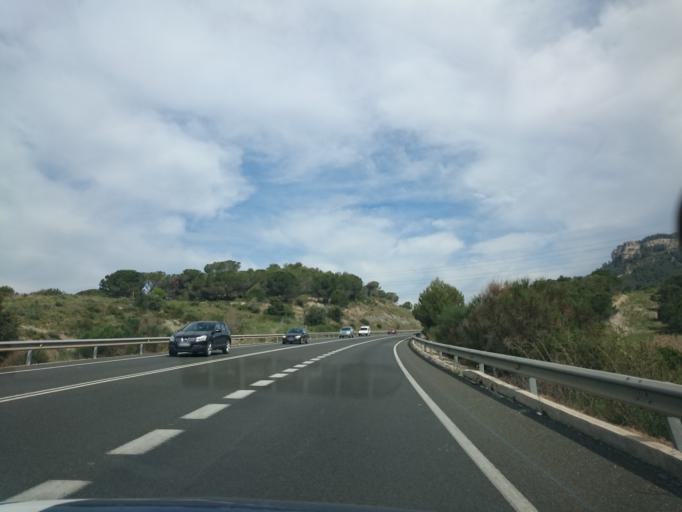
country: ES
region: Catalonia
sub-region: Provincia de Barcelona
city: La Pobla de Claramunt
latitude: 41.5586
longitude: 1.6812
